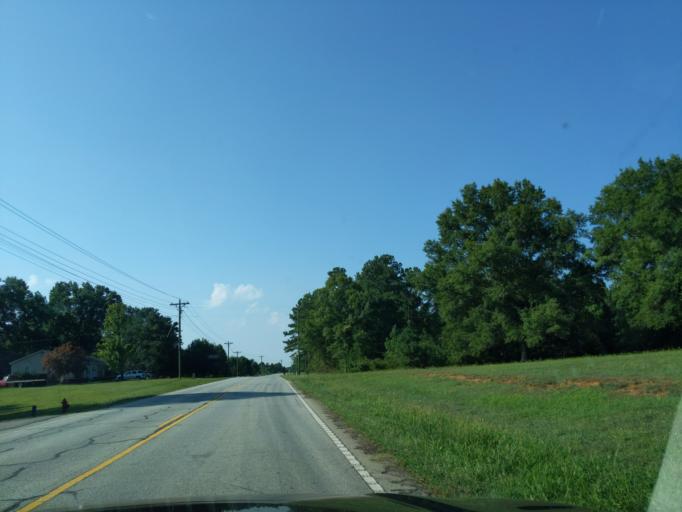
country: US
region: South Carolina
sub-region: Newberry County
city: Prosperity
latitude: 34.1725
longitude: -81.5340
